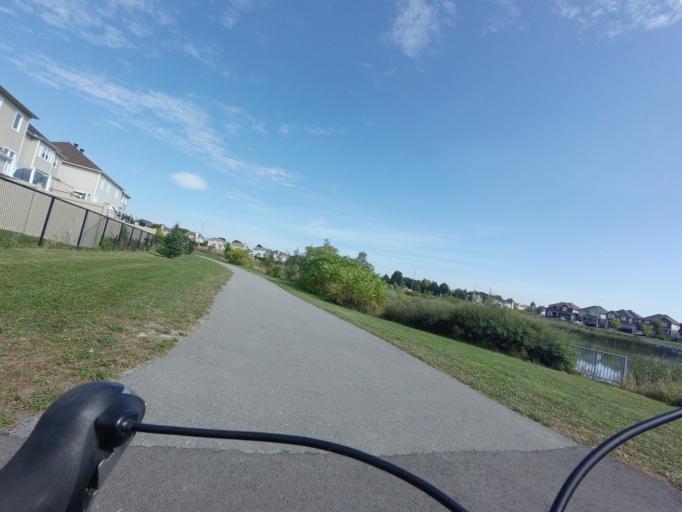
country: CA
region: Ontario
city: Bells Corners
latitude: 45.2715
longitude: -75.7774
